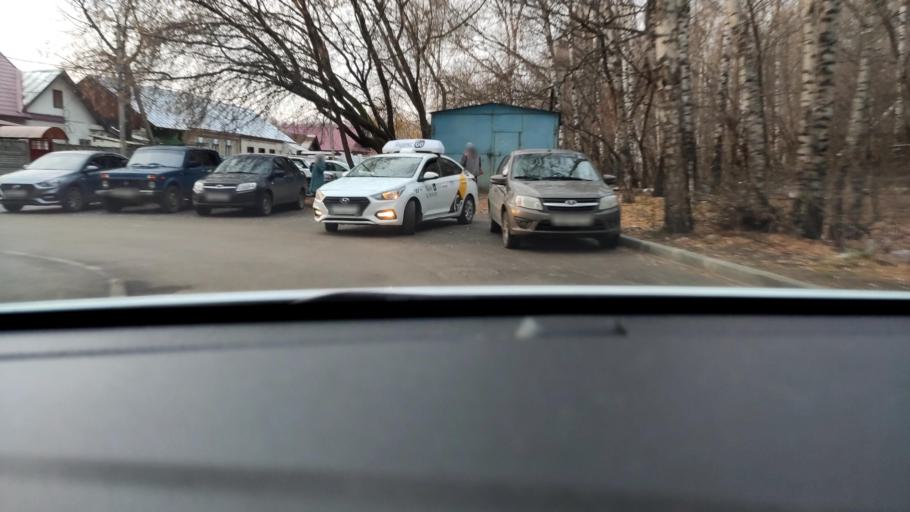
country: RU
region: Tatarstan
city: Staroye Arakchino
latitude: 55.8437
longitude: 49.0351
